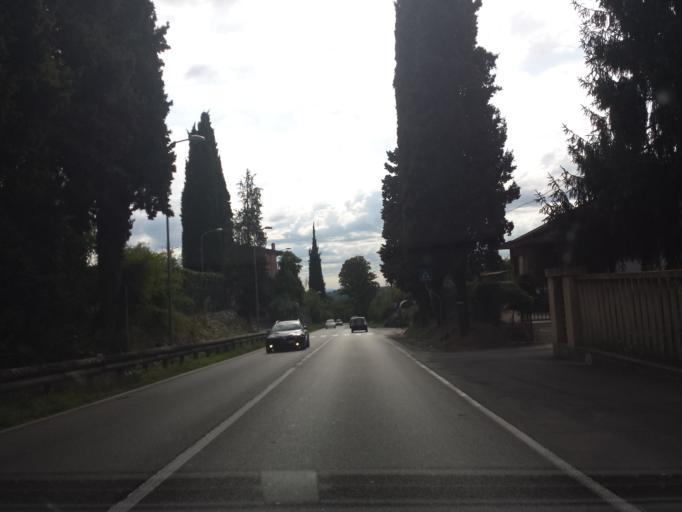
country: IT
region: Lombardy
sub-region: Provincia di Brescia
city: Roe Volciano
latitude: 45.6111
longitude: 10.4927
